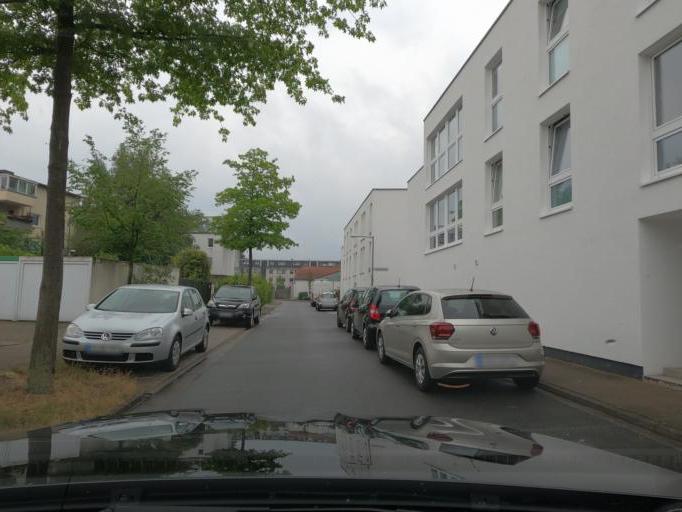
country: DE
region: Lower Saxony
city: Isernhagen Farster Bauerschaft
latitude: 52.3956
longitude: 9.8443
